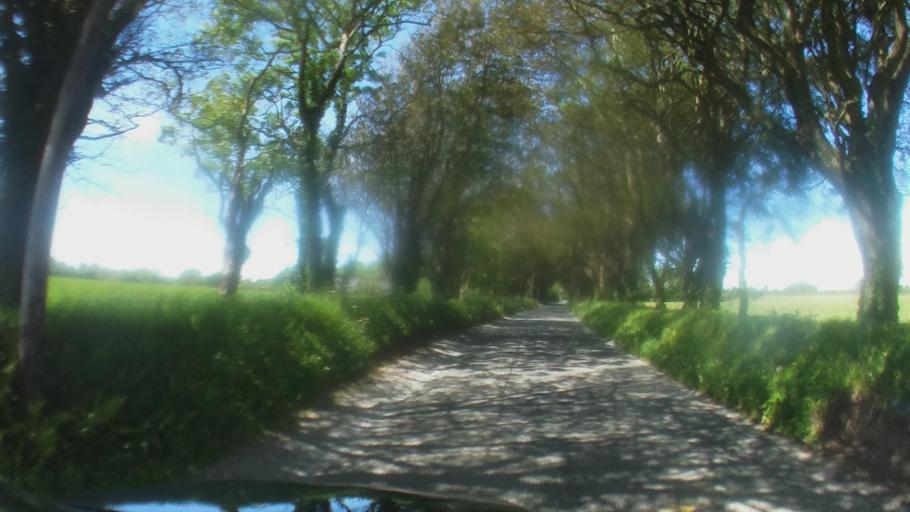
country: IE
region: Leinster
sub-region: Loch Garman
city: Loch Garman
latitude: 52.2327
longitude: -6.5610
